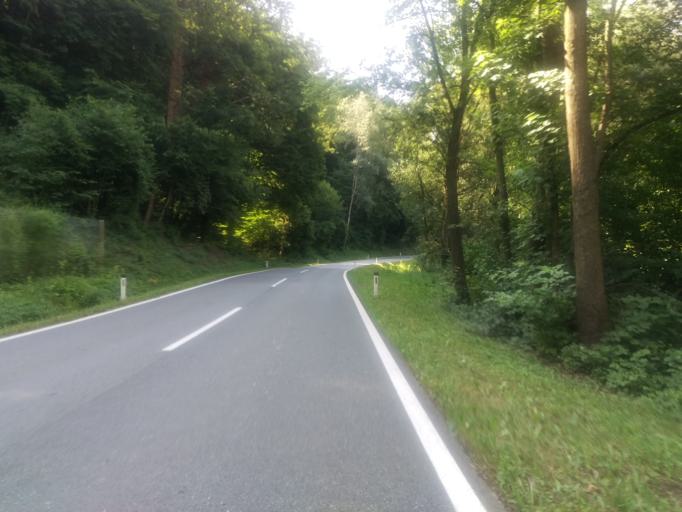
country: AT
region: Styria
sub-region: Politischer Bezirk Graz-Umgebung
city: Mellach
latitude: 46.9440
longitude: 15.5119
